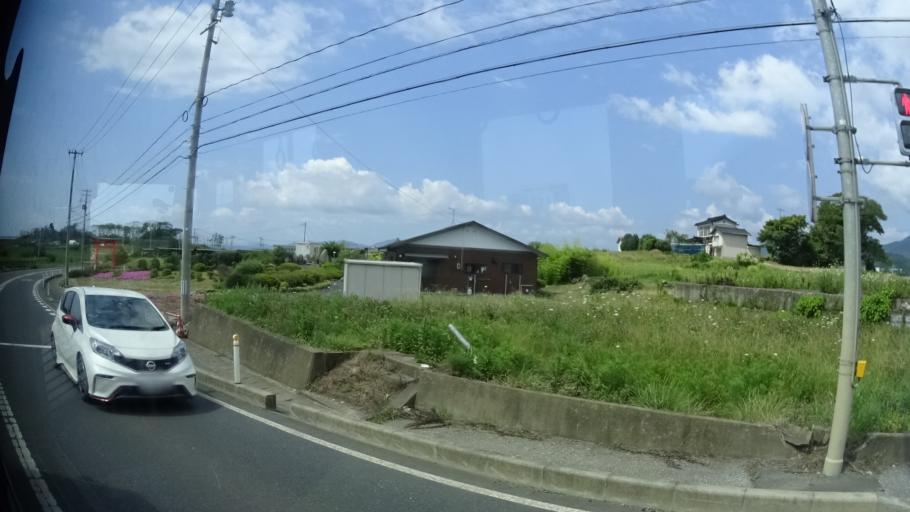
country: JP
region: Iwate
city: Ofunato
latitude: 38.8159
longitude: 141.5733
